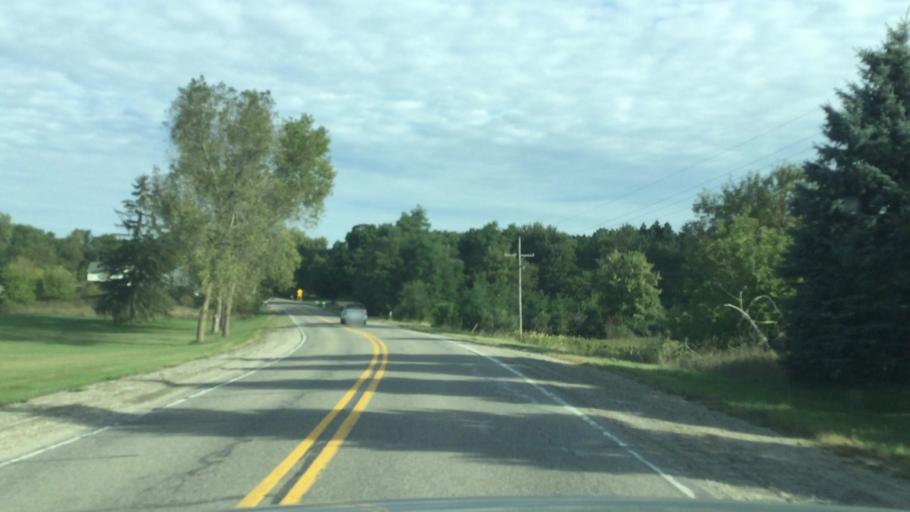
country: US
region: Michigan
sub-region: Livingston County
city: Howell
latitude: 42.5725
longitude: -83.8931
